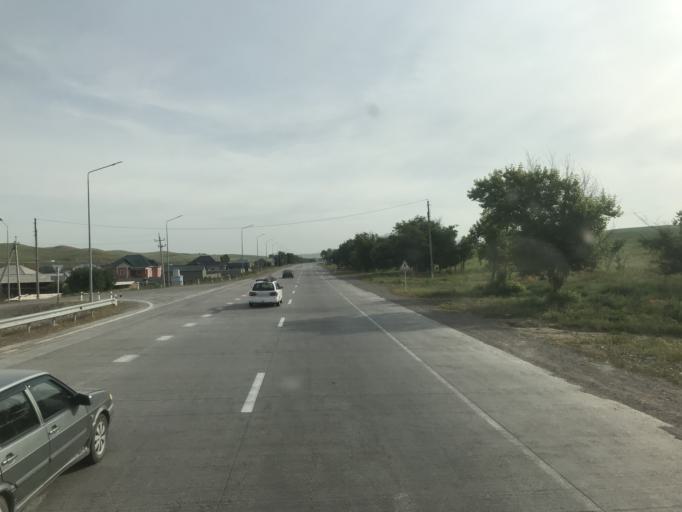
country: KZ
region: Ongtustik Qazaqstan
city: Qazyqurt
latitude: 41.9055
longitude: 69.4648
